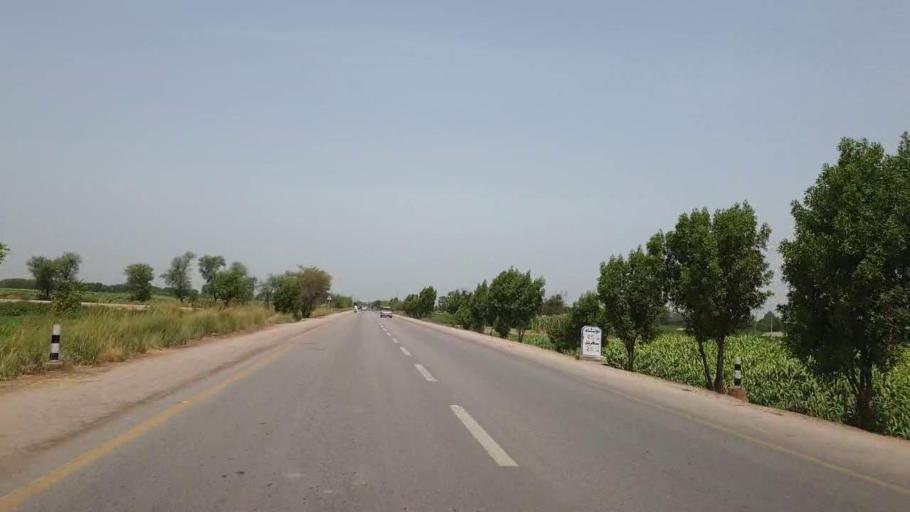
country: PK
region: Sindh
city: Nawabshah
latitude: 26.2349
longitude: 68.4790
